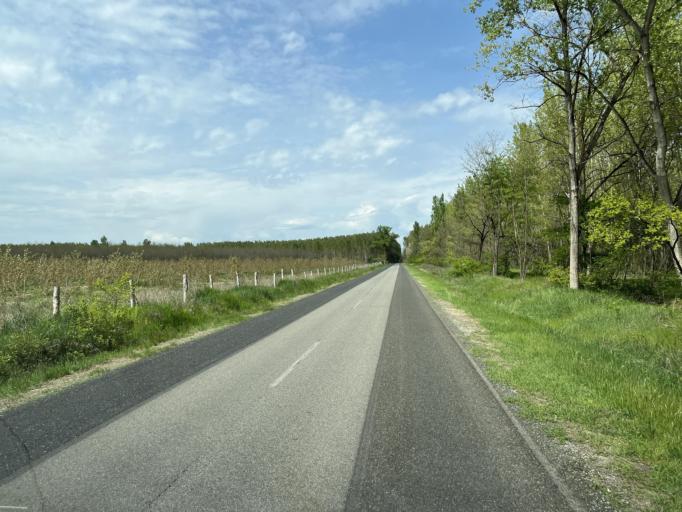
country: HU
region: Pest
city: Albertirsa
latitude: 47.1850
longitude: 19.6130
